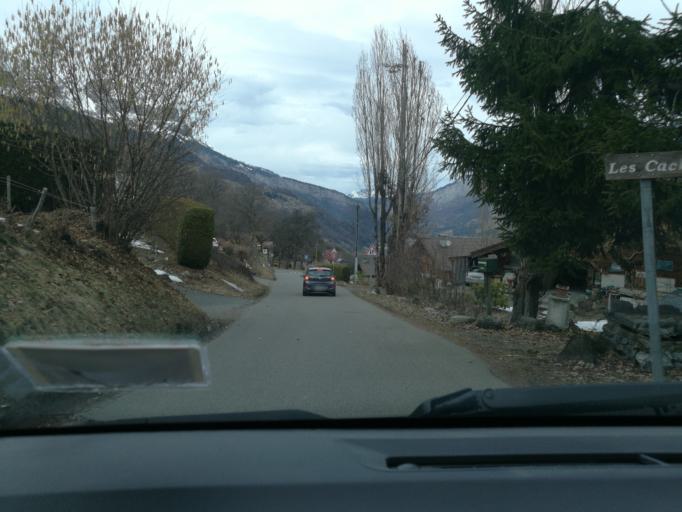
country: FR
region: Rhone-Alpes
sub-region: Departement de la Haute-Savoie
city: Cordon
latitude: 45.9202
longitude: 6.6286
